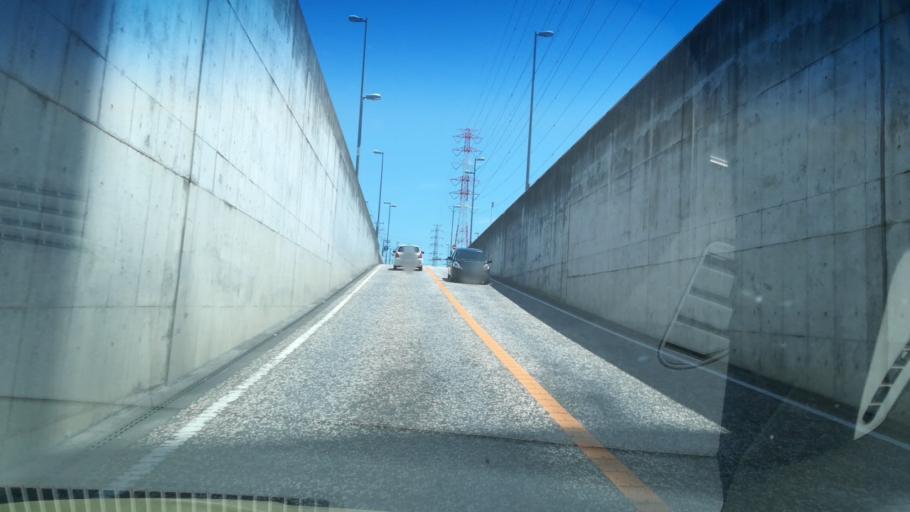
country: JP
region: Tokyo
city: Hachioji
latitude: 35.5881
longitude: 139.3532
